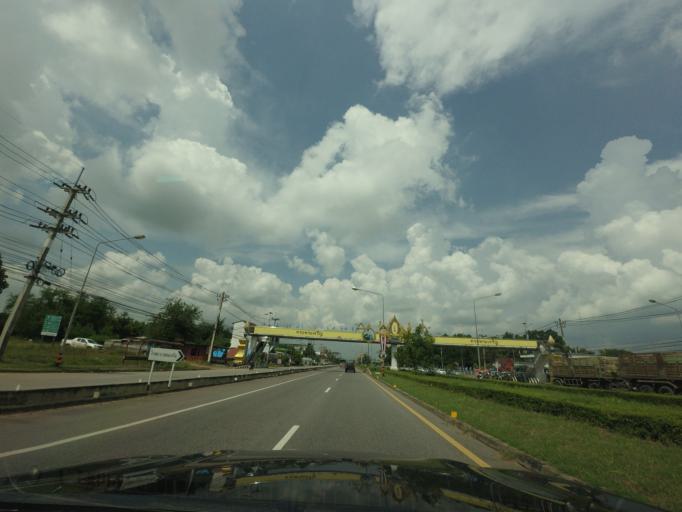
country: TH
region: Khon Kaen
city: Nong Ruea
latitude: 16.4904
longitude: 102.4438
